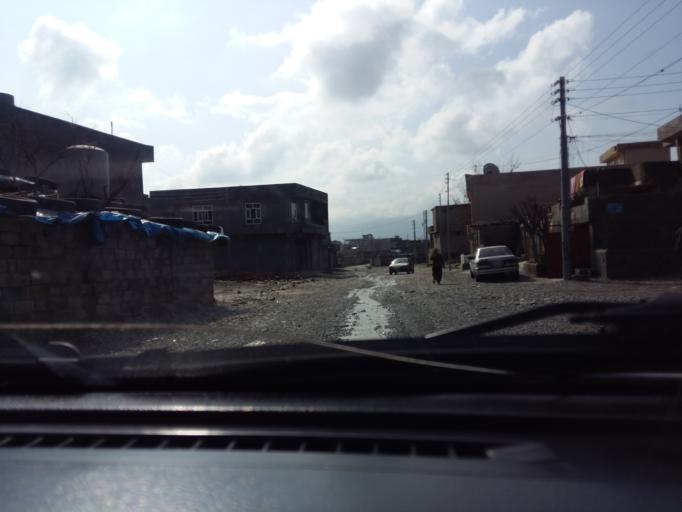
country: IQ
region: As Sulaymaniyah
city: Qeladize
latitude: 36.1933
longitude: 45.1233
